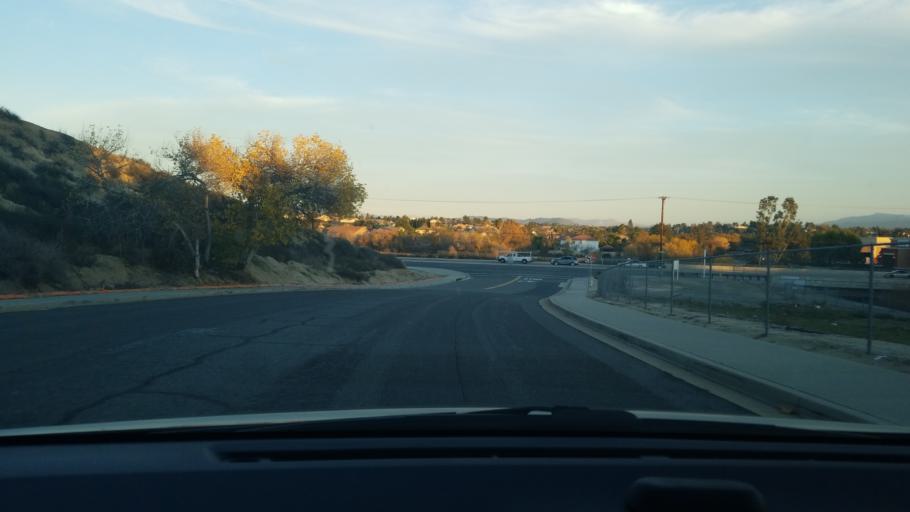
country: US
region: California
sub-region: Riverside County
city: Murrieta Hot Springs
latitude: 33.5429
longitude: -117.1449
